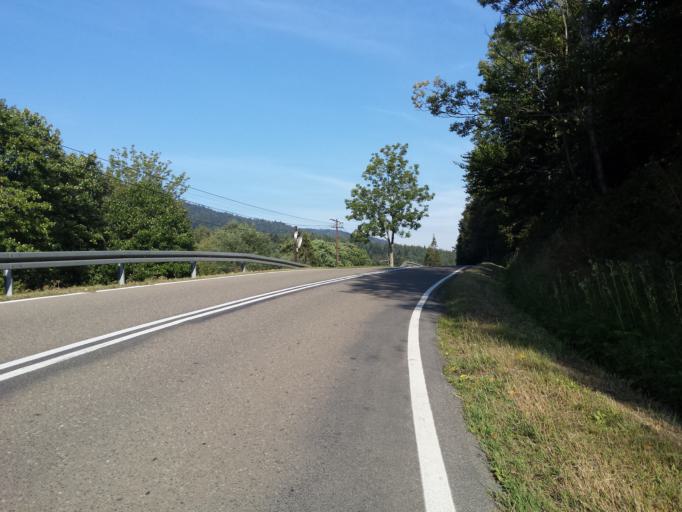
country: PL
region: Subcarpathian Voivodeship
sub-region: Powiat leski
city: Cisna
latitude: 49.2181
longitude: 22.3187
